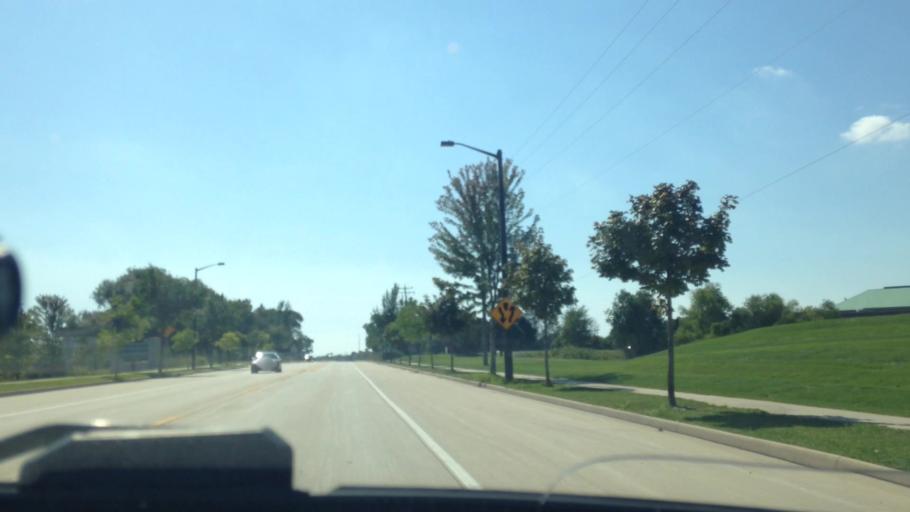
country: US
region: Wisconsin
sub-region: Ozaukee County
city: Port Washington
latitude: 43.3745
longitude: -87.8951
